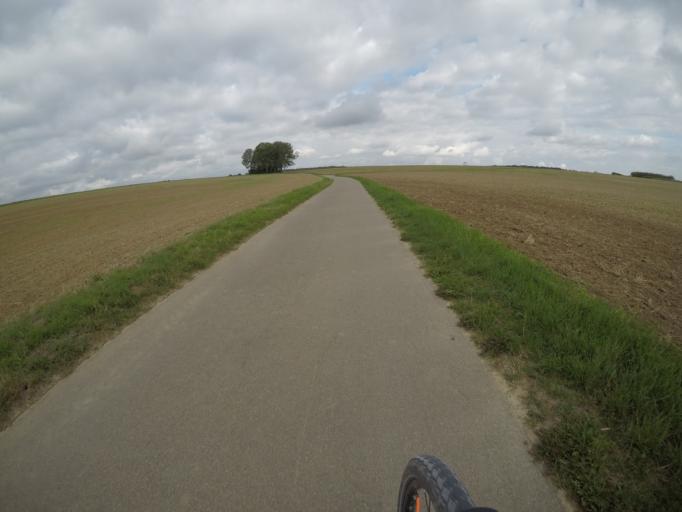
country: DE
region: Baden-Wuerttemberg
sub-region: Regierungsbezirk Stuttgart
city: Renningen
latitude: 48.7369
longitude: 8.9300
